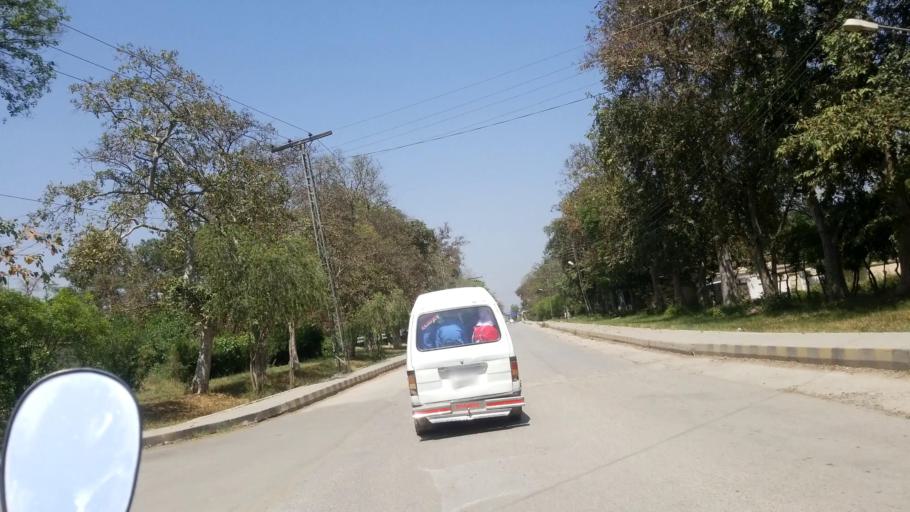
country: PK
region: Khyber Pakhtunkhwa
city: Peshawar
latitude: 34.0154
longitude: 71.4835
